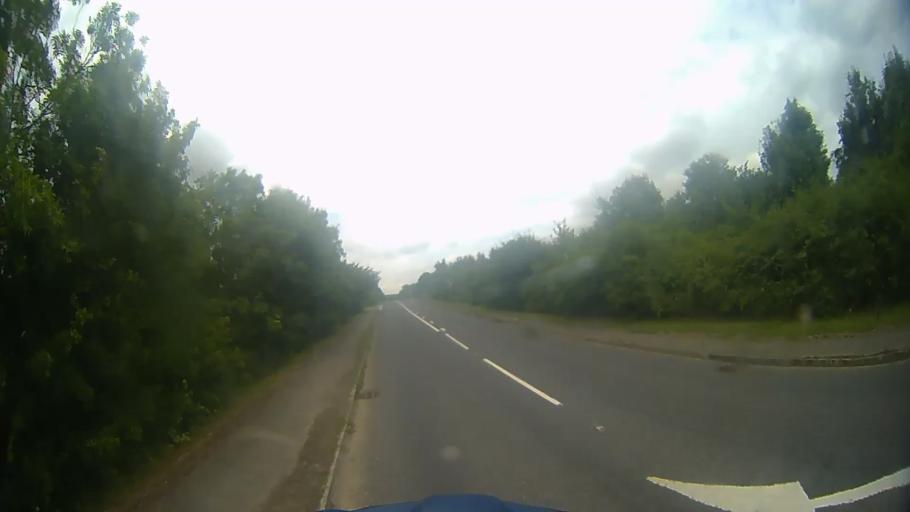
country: GB
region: England
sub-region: Hampshire
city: Kingsley
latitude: 51.1855
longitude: -0.8780
